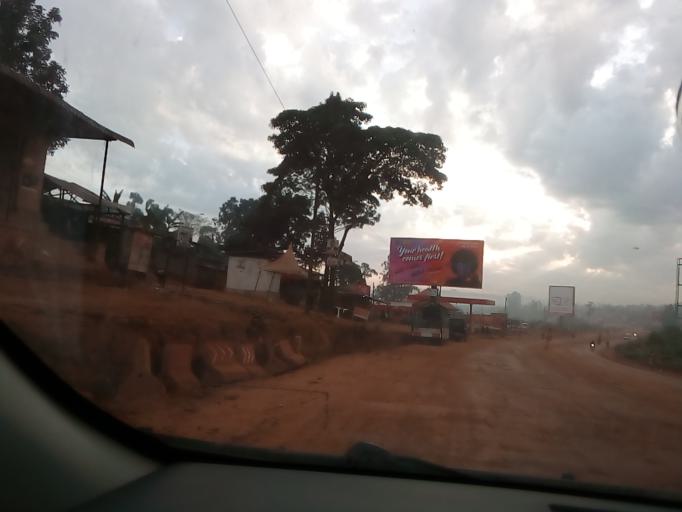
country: UG
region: Central Region
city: Masaka
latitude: -0.3295
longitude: 31.7468
